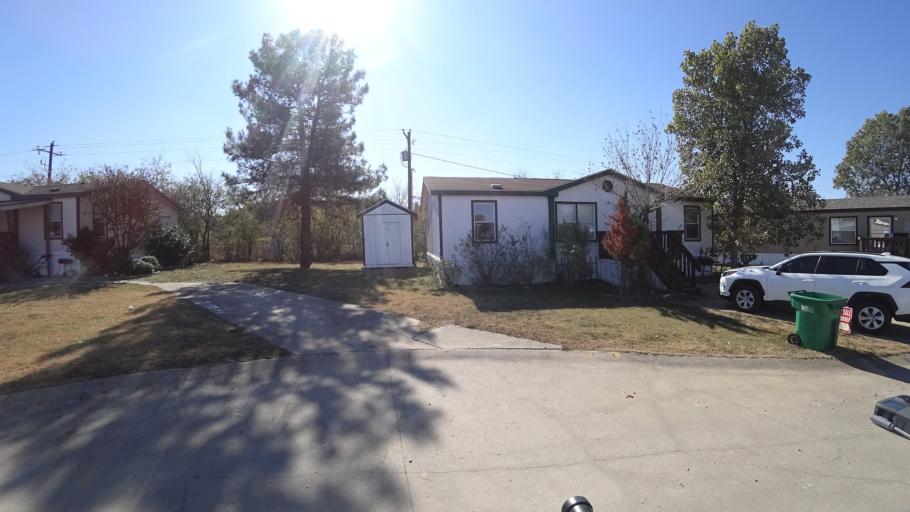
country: US
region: Texas
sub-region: Denton County
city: Lewisville
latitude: 33.0396
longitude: -96.9340
